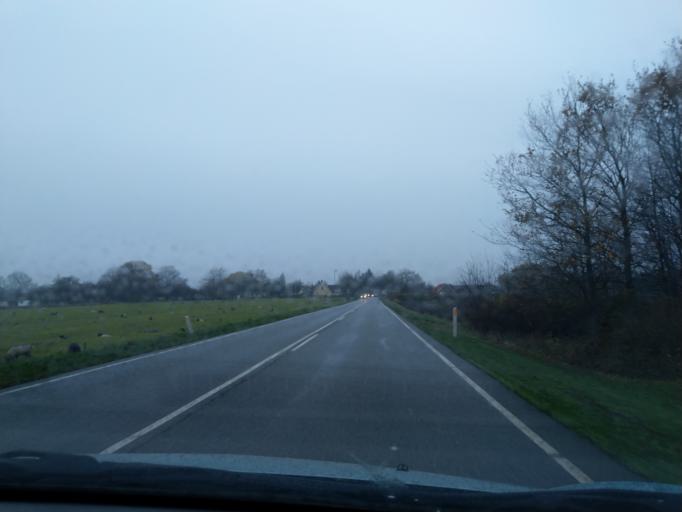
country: DK
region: Zealand
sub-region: Vordingborg Kommune
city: Orslev
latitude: 55.1232
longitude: 11.9589
